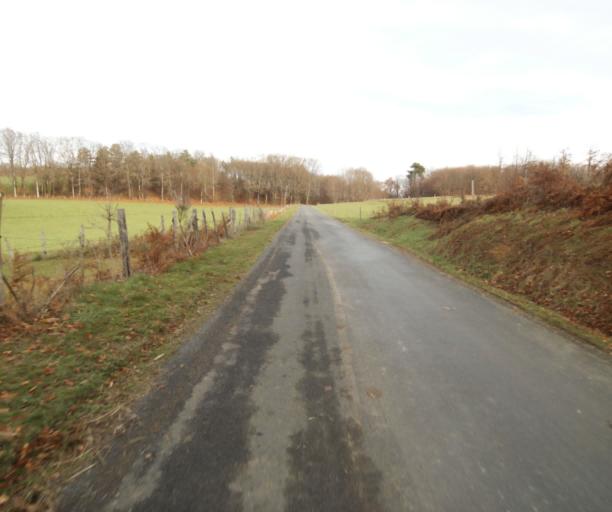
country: FR
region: Limousin
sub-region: Departement de la Correze
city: Chameyrat
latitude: 45.2501
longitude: 1.6966
